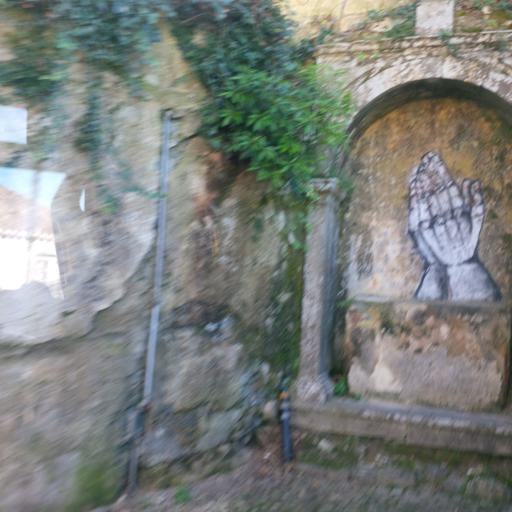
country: PT
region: Lisbon
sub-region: Sintra
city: Sintra
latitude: 38.7959
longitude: -9.3924
